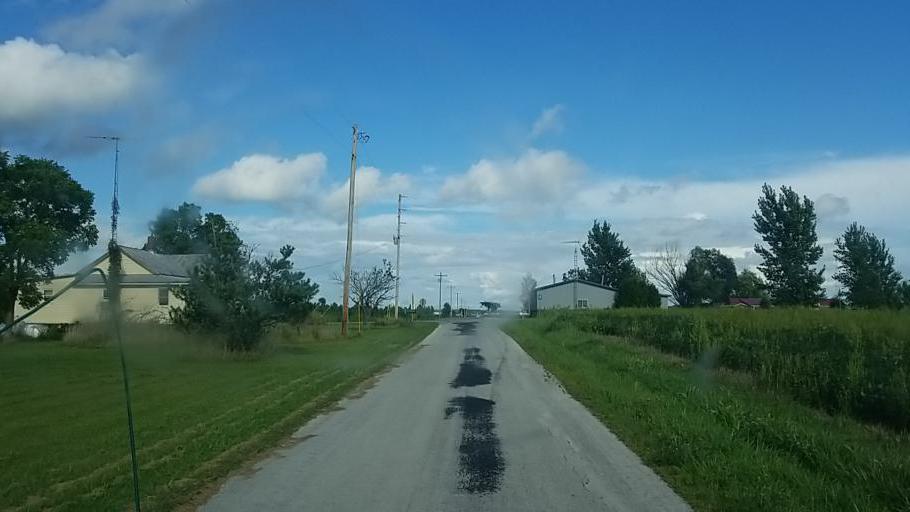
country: US
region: Ohio
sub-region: Hardin County
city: Forest
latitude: 40.7450
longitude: -83.4975
